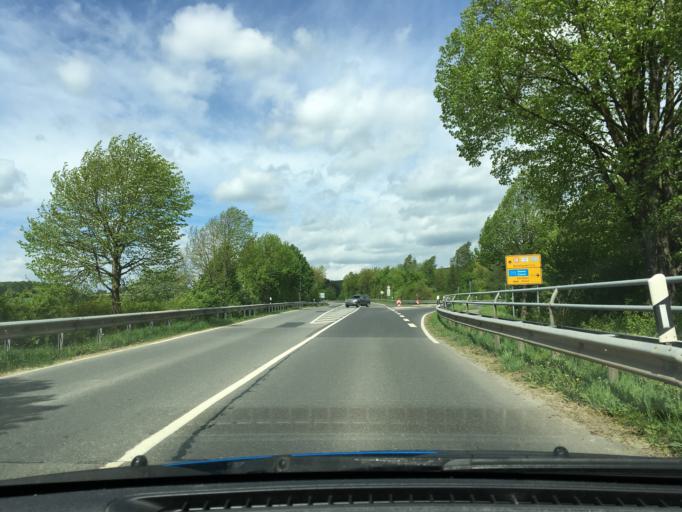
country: DE
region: Lower Saxony
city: Einbeck
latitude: 51.8314
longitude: 9.8347
